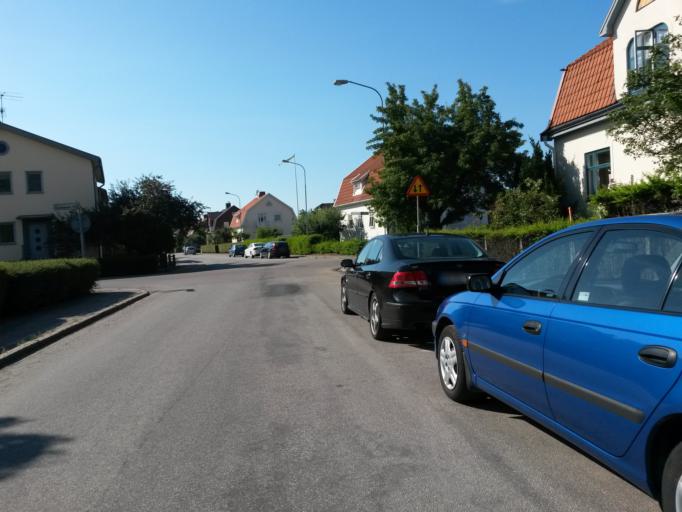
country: SE
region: Vaestra Goetaland
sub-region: Lidkopings Kommun
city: Lidkoping
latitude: 58.5057
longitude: 13.1534
